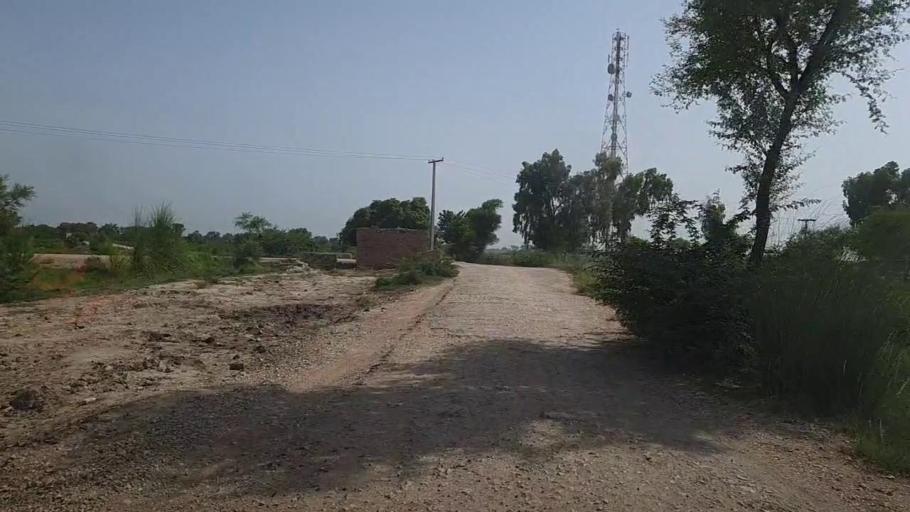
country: PK
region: Sindh
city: Pad Idan
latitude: 26.7813
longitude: 68.3230
